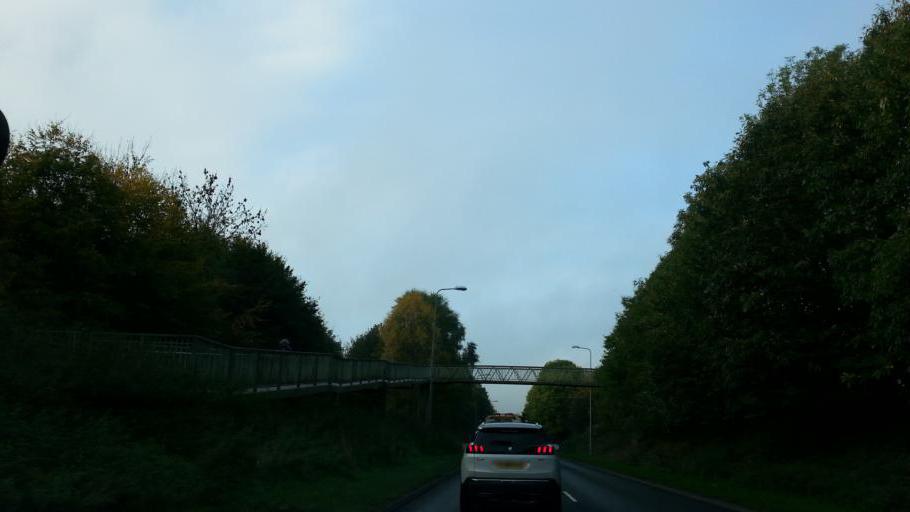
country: GB
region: England
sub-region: Worcestershire
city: Bromsgrove
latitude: 52.3324
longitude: -2.0491
